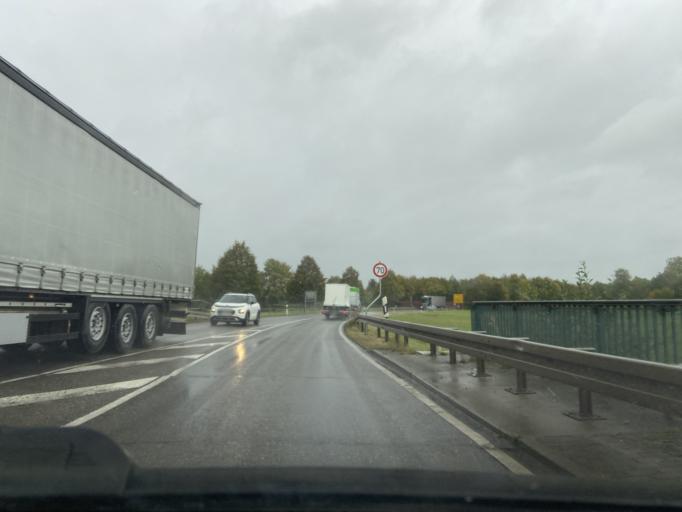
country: DE
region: Baden-Wuerttemberg
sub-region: Tuebingen Region
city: Ennetach
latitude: 48.0488
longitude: 9.3216
